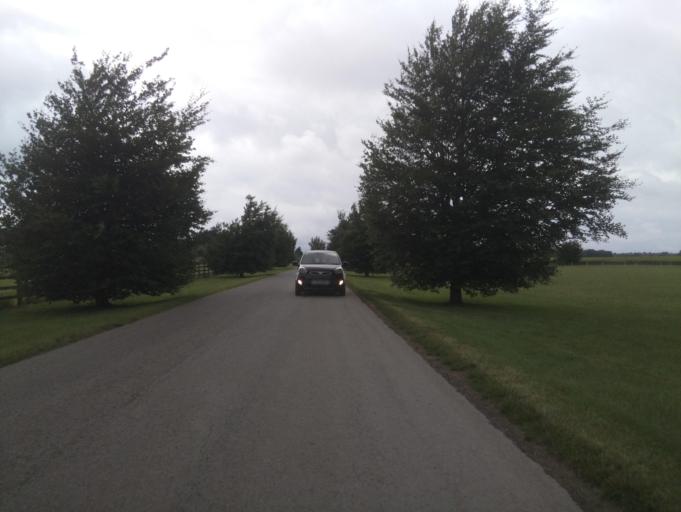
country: GB
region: England
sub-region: South Gloucestershire
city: Cold Ashton
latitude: 51.4197
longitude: -2.3988
